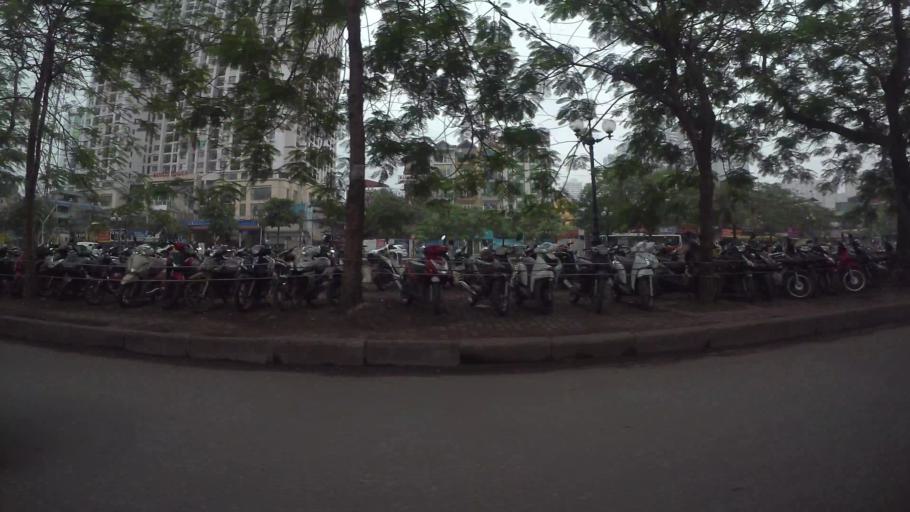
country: VN
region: Ha Noi
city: Hai BaTrung
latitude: 20.9942
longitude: 105.8623
